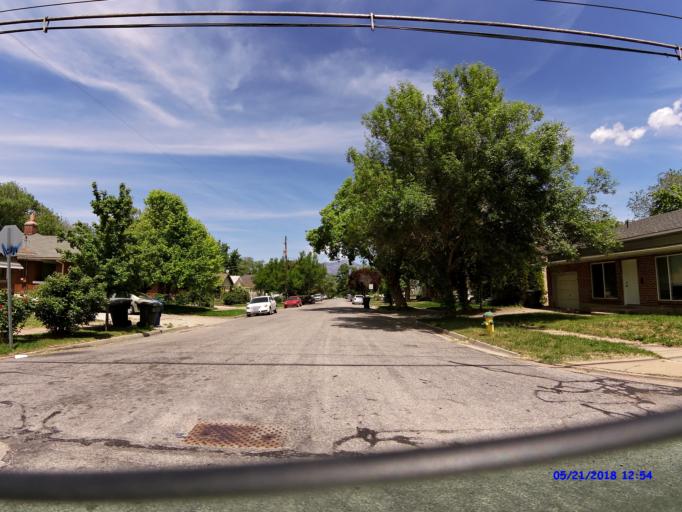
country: US
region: Utah
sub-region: Weber County
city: South Ogden
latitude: 41.1978
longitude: -111.9667
